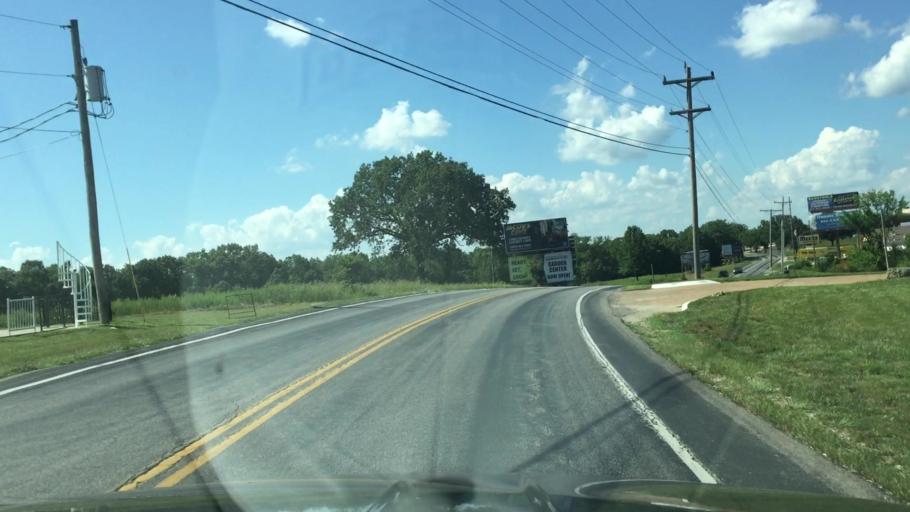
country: US
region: Missouri
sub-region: Camden County
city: Osage Beach
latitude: 38.1410
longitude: -92.5912
